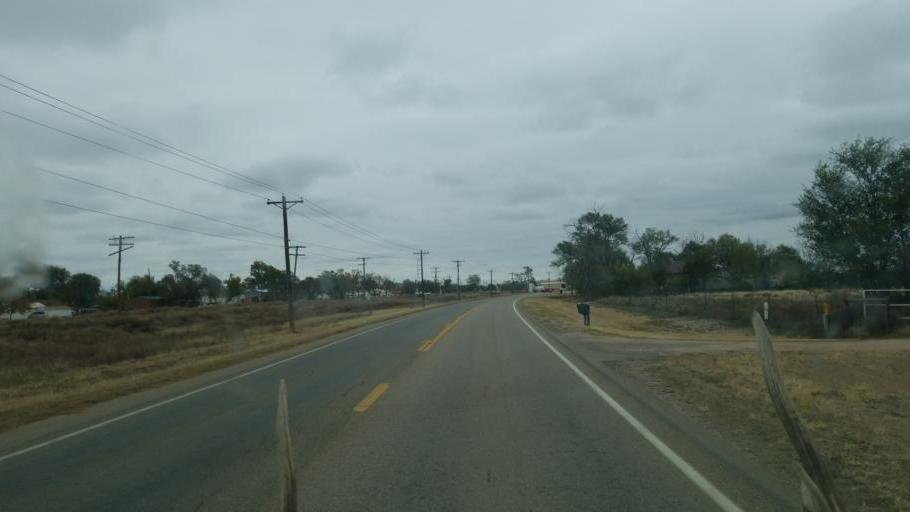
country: US
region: Colorado
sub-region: Crowley County
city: Ordway
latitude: 38.2139
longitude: -103.7616
